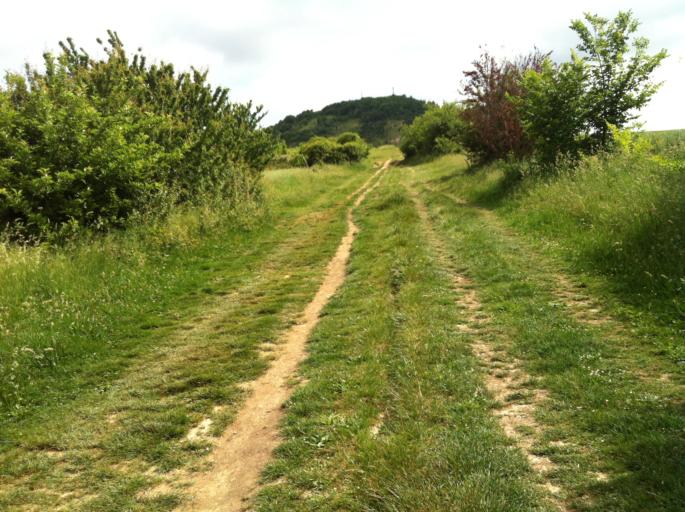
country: ES
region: Basque Country
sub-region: Provincia de Alava
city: Gasteiz / Vitoria
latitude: 42.8237
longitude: -2.6611
